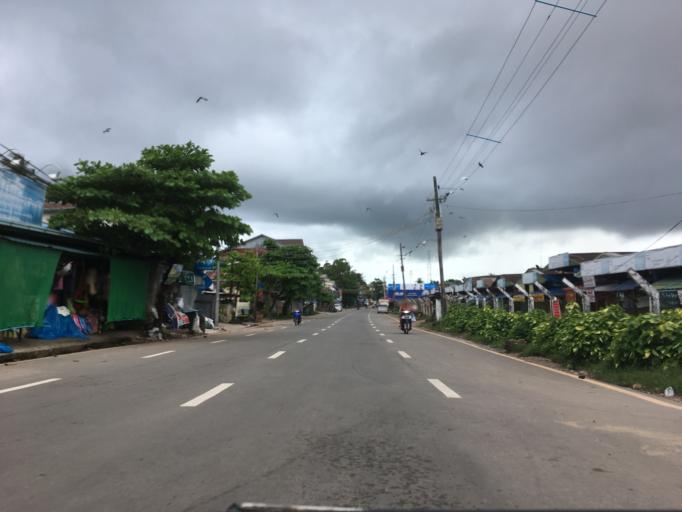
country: MM
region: Mon
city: Mawlamyine
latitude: 16.4660
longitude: 97.6237
